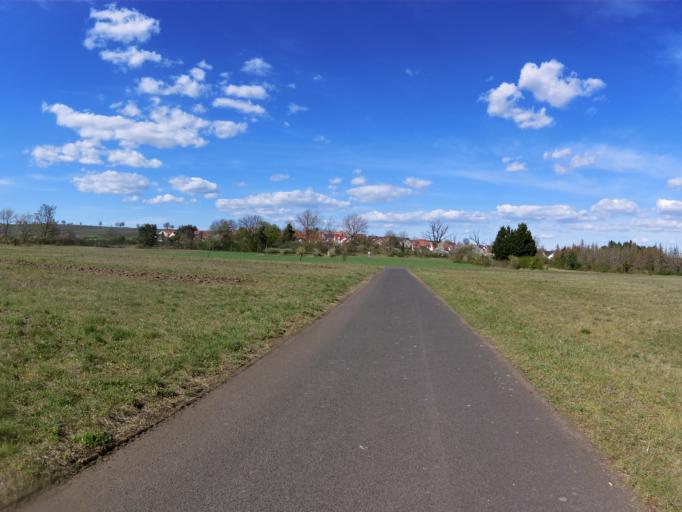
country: DE
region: Bavaria
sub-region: Regierungsbezirk Unterfranken
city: Volkach
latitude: 49.8572
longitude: 10.2115
